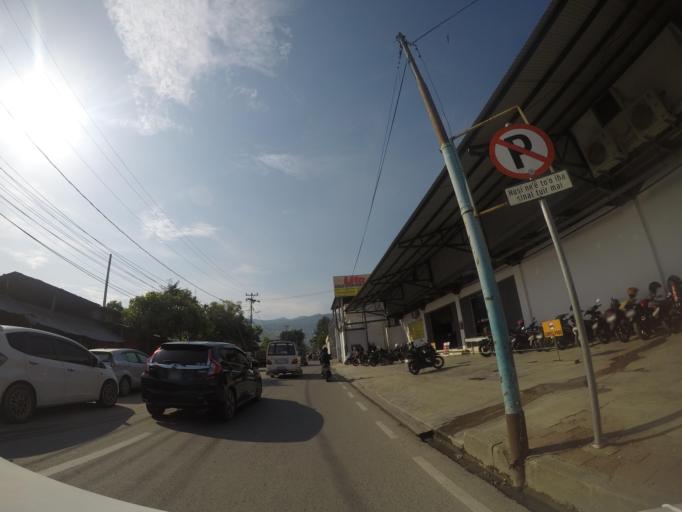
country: TL
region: Dili
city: Dili
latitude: -8.5510
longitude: 125.5900
